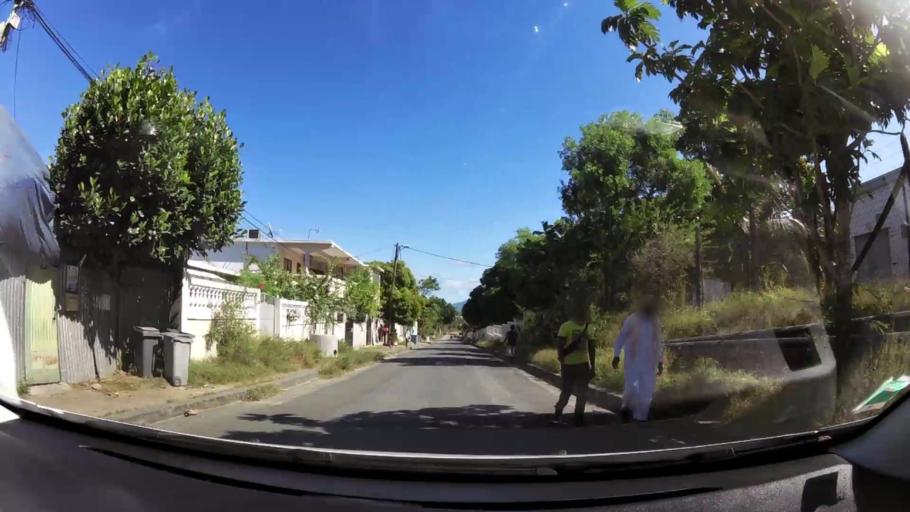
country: YT
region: Pamandzi
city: Pamandzi
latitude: -12.7833
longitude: 45.2760
